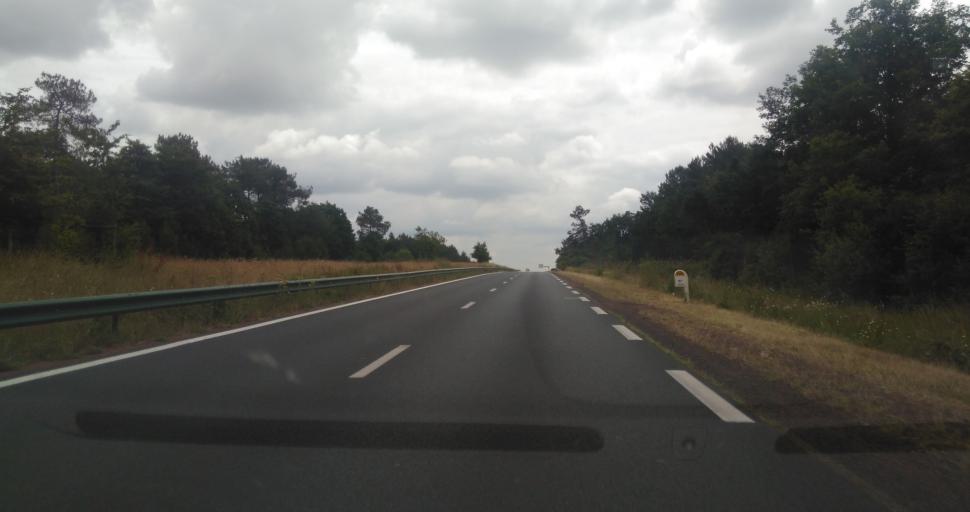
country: FR
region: Pays de la Loire
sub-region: Departement de la Vendee
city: Bournezeau
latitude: 46.6480
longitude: -1.2133
